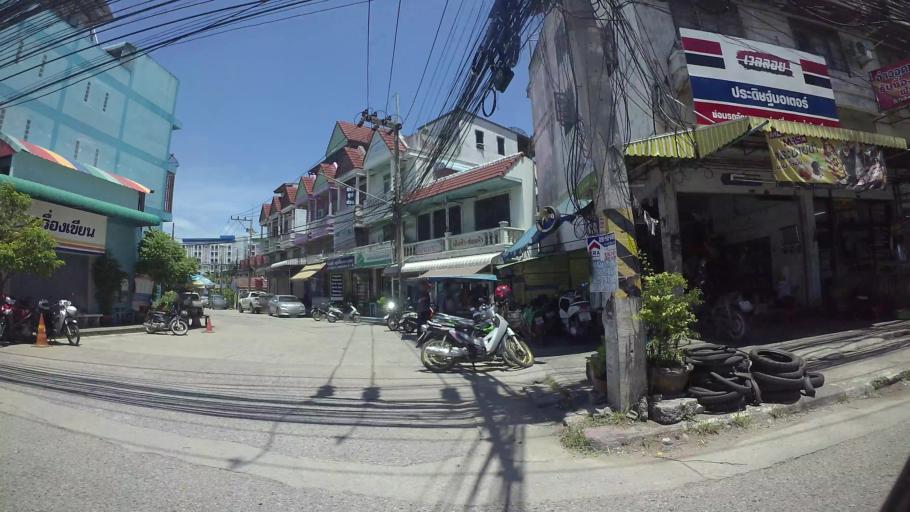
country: TH
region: Chon Buri
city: Si Racha
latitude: 13.1142
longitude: 100.9249
